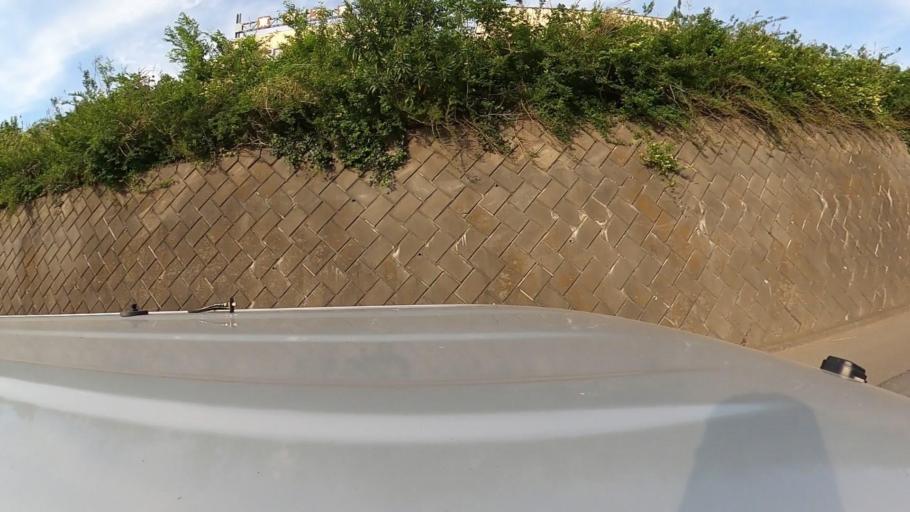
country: JP
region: Saitama
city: Oi
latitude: 35.8301
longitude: 139.5096
